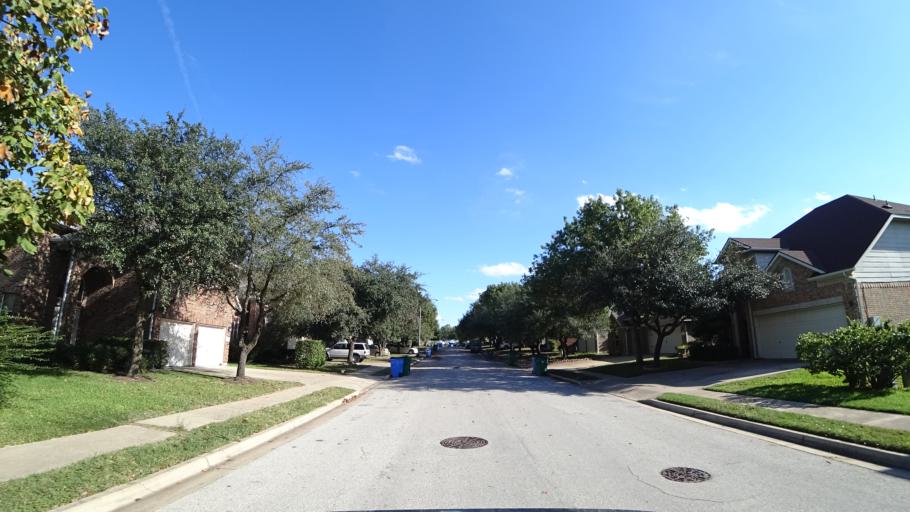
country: US
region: Texas
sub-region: Travis County
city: Wells Branch
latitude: 30.4617
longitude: -97.6820
